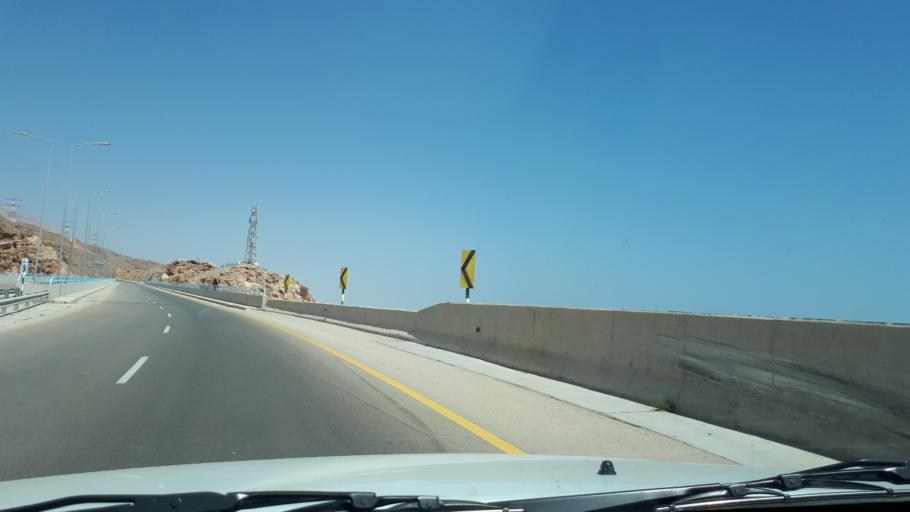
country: OM
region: Ash Sharqiyah
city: Sur
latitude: 22.8214
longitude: 59.2611
